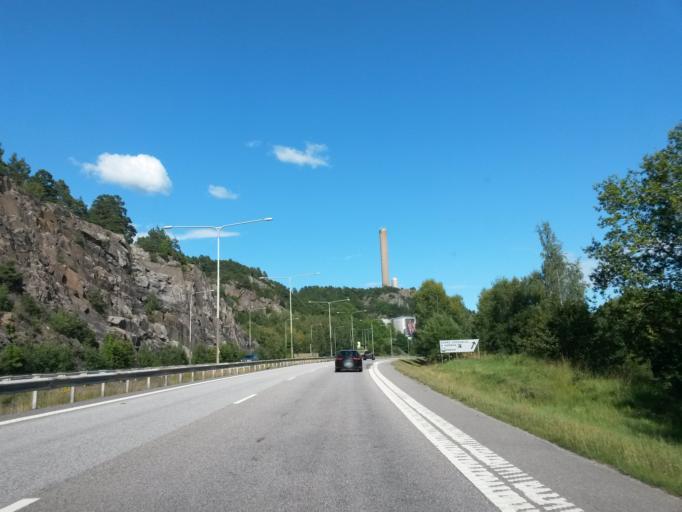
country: SE
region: Vaestra Goetaland
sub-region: Uddevalla Kommun
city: Uddevalla
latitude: 58.3562
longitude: 11.9054
